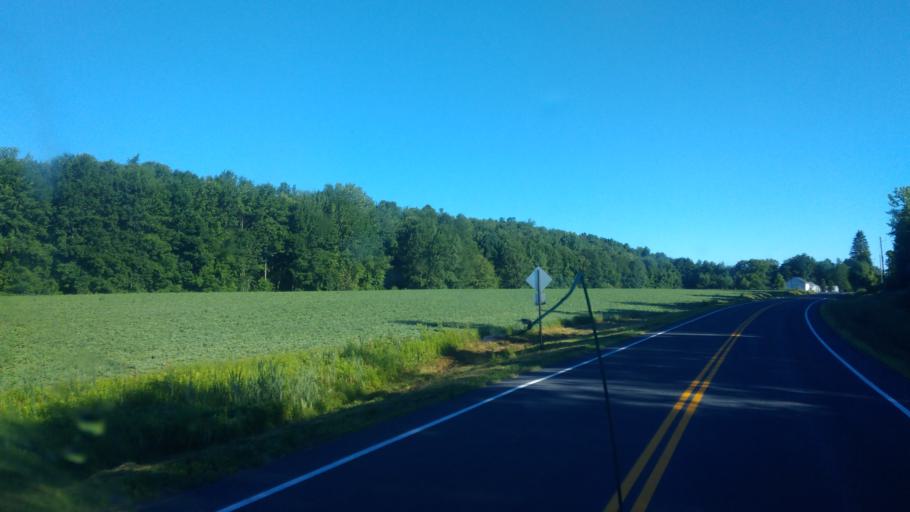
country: US
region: New York
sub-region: Wayne County
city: Sodus
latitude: 43.1556
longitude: -77.0492
